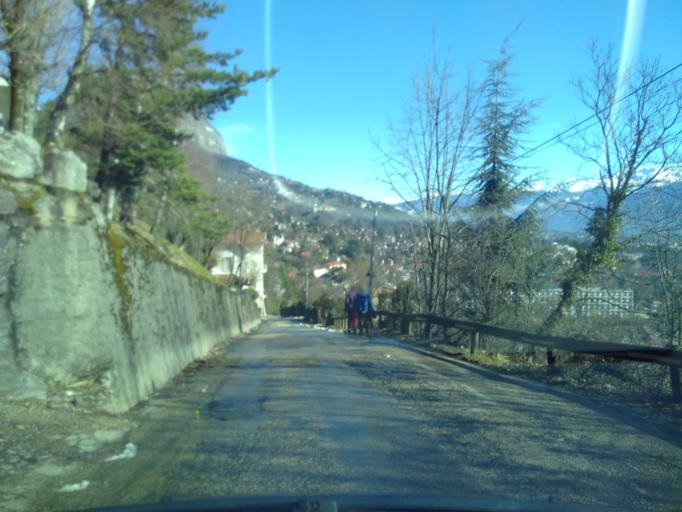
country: FR
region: Rhone-Alpes
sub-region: Departement de l'Isere
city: La Tronche
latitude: 45.2022
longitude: 5.7318
